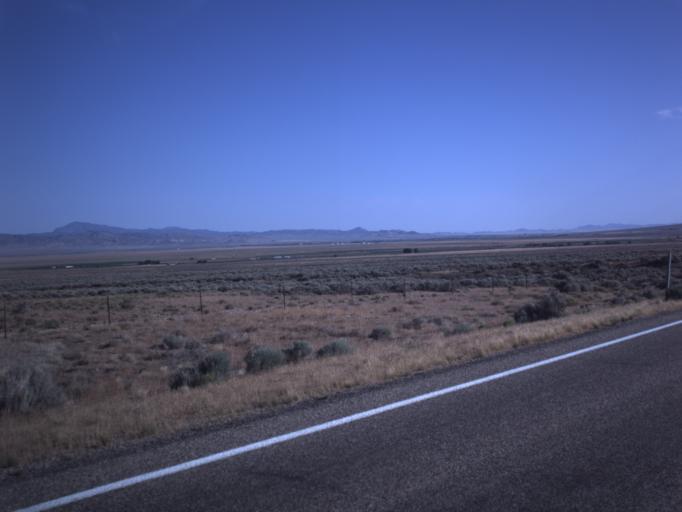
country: US
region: Utah
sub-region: Beaver County
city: Milford
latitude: 38.1684
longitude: -112.9536
